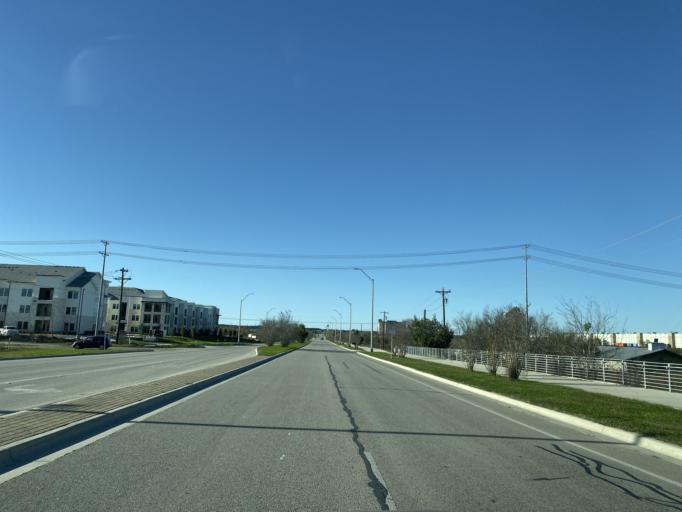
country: US
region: Texas
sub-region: Guadalupe County
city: Redwood
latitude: 29.8299
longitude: -97.9609
